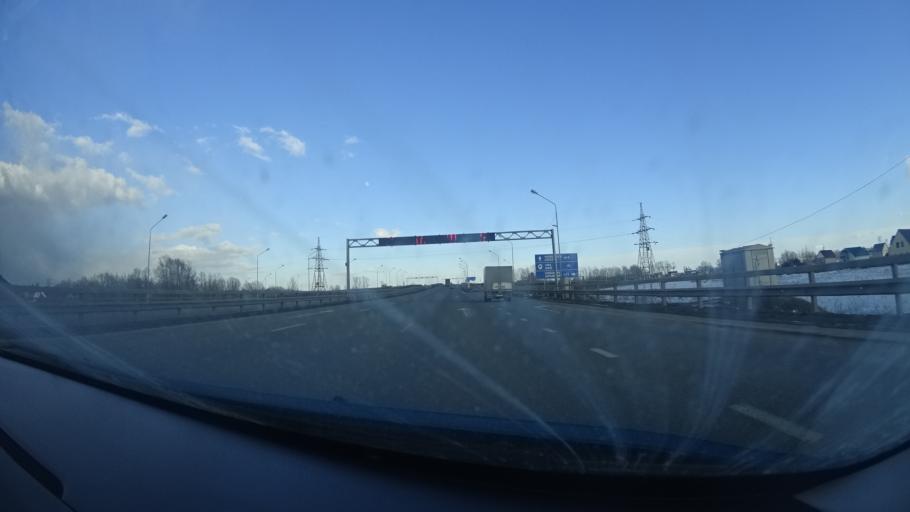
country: RU
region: Bashkortostan
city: Ufa
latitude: 54.6453
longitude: 55.9256
